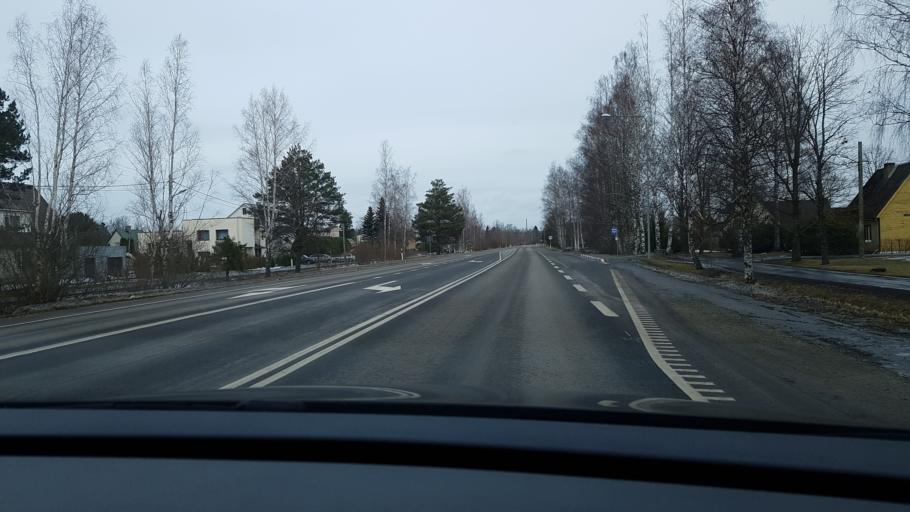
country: EE
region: Paernumaa
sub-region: Sindi linn
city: Sindi
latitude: 58.3965
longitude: 24.6472
